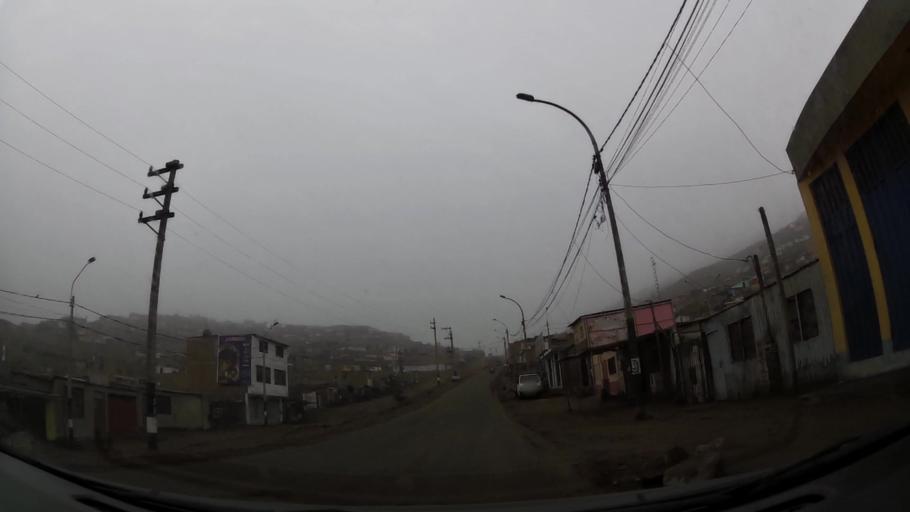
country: PE
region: Lima
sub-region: Lima
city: Santa Rosa
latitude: -11.8218
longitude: -77.1381
